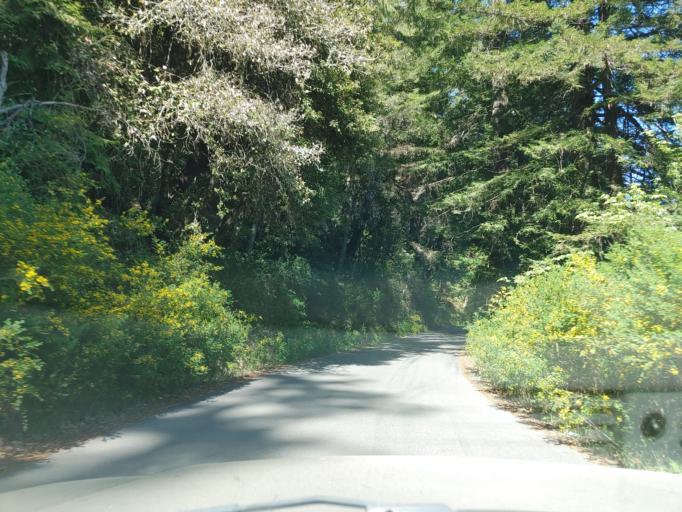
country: US
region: California
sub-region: Humboldt County
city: Rio Dell
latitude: 40.3543
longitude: -123.9302
